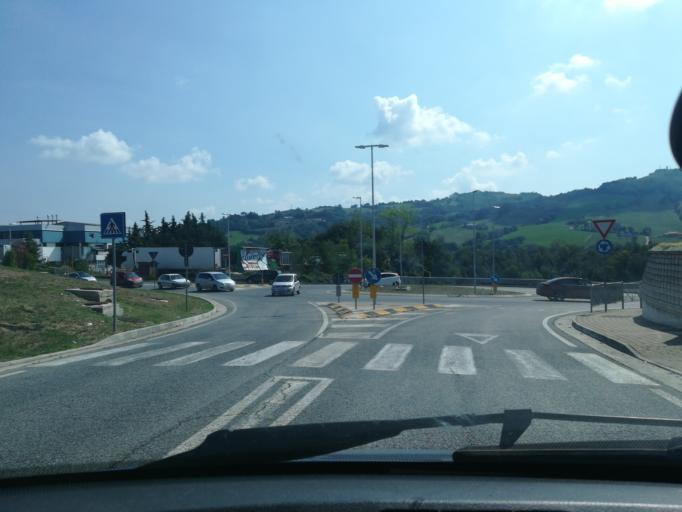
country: IT
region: The Marches
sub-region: Provincia di Macerata
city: Tolentino
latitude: 43.2160
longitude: 13.3085
